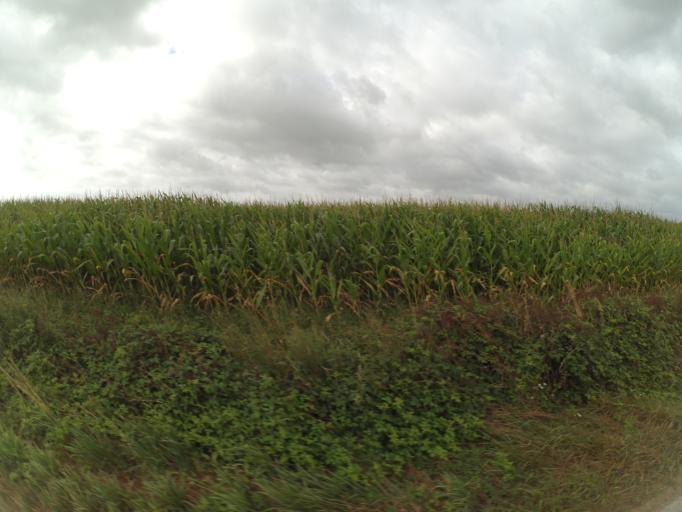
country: FR
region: Pays de la Loire
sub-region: Departement de Maine-et-Loire
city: Saint-Crespin-sur-Moine
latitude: 47.0810
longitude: -1.1770
